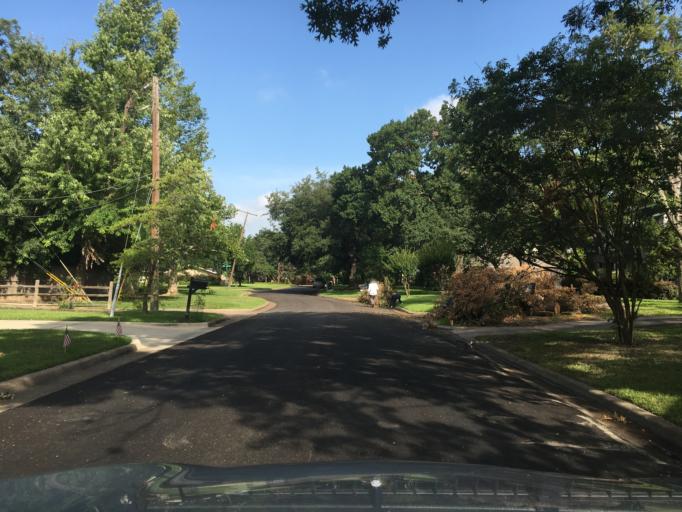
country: US
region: Texas
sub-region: Dallas County
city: Richardson
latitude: 32.9303
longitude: -96.7810
